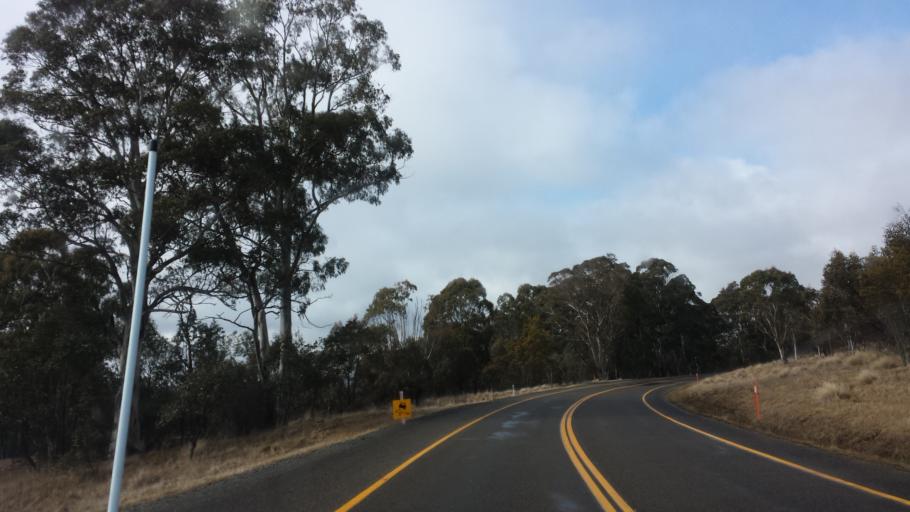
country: AU
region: Victoria
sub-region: Alpine
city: Mount Beauty
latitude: -37.0578
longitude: 147.3318
